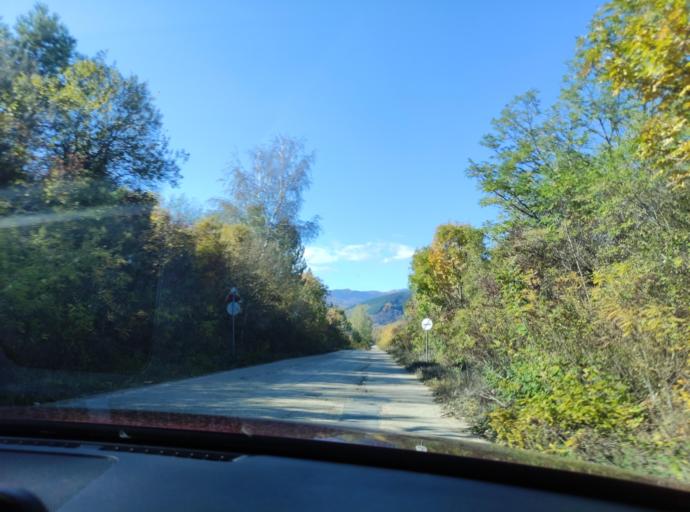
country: BG
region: Montana
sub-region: Obshtina Chiprovtsi
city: Chiprovtsi
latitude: 43.3791
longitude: 22.9127
